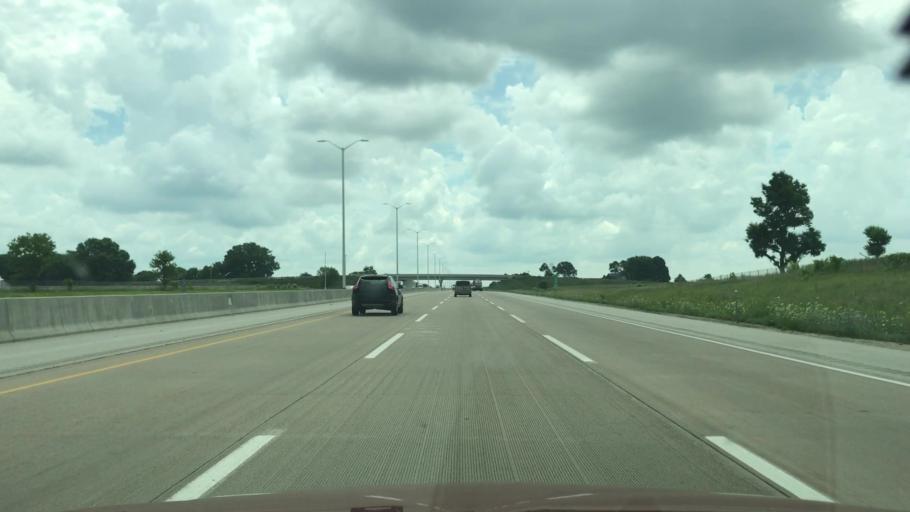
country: US
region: Illinois
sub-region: Boone County
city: Belvidere
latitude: 42.2270
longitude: -88.7686
